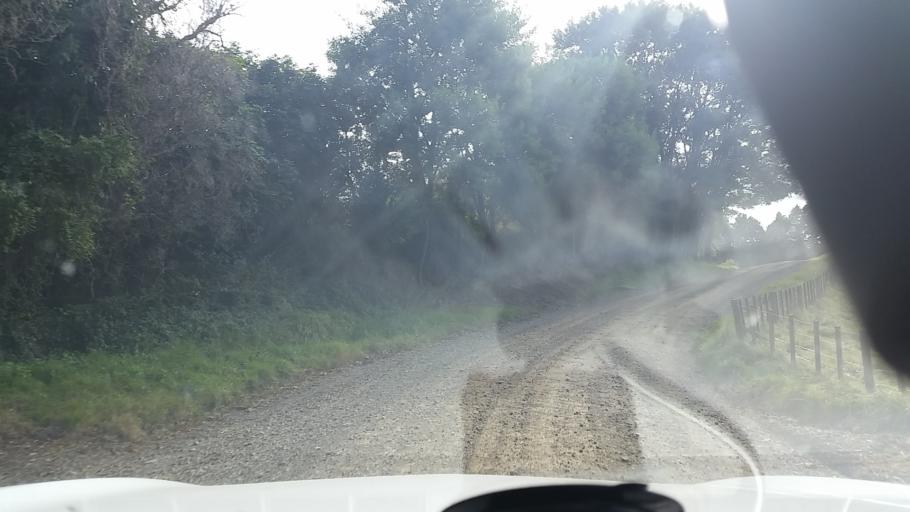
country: NZ
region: Hawke's Bay
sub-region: Napier City
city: Napier
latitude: -39.1332
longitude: 176.8956
